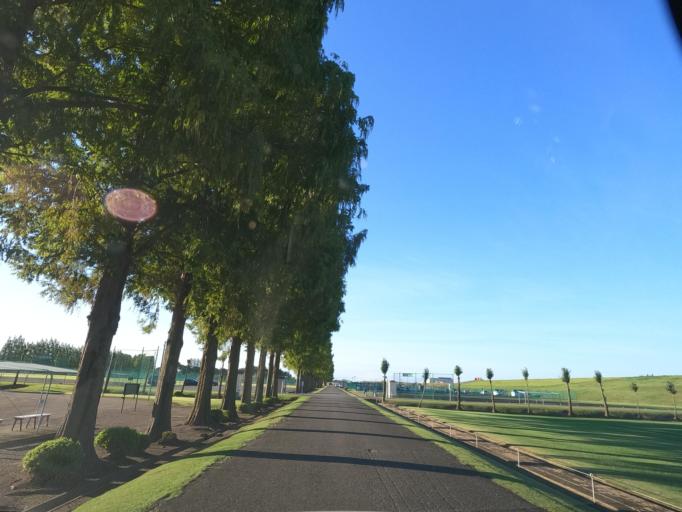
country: JP
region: Saitama
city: Shiki
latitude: 35.8890
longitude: 139.5764
